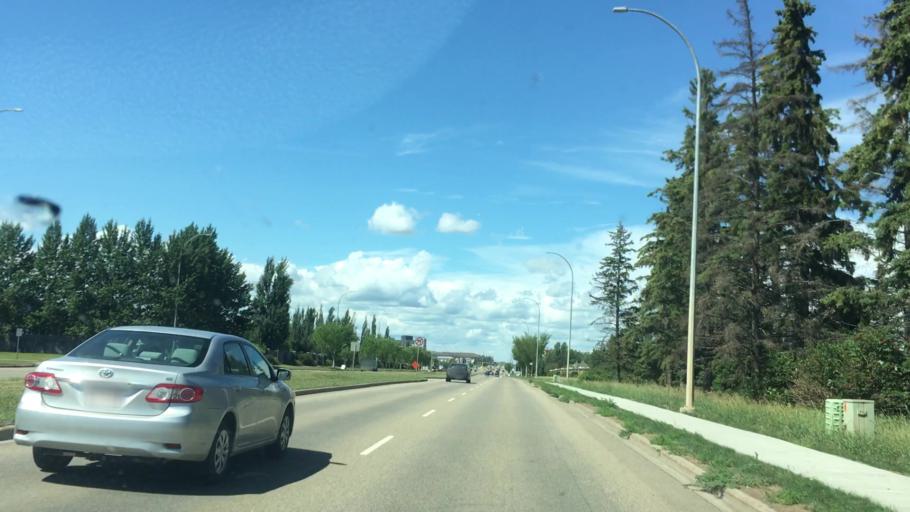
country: CA
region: Alberta
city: Beaumont
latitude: 53.4249
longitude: -113.5028
